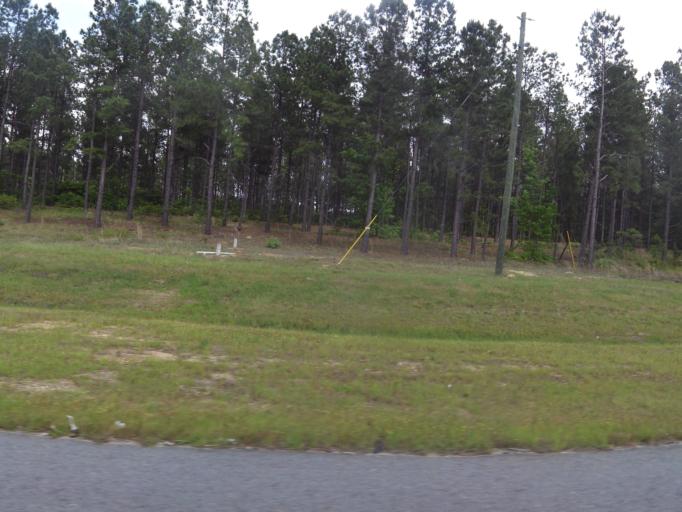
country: US
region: Georgia
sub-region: Emanuel County
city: Swainsboro
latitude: 32.7228
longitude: -82.3944
